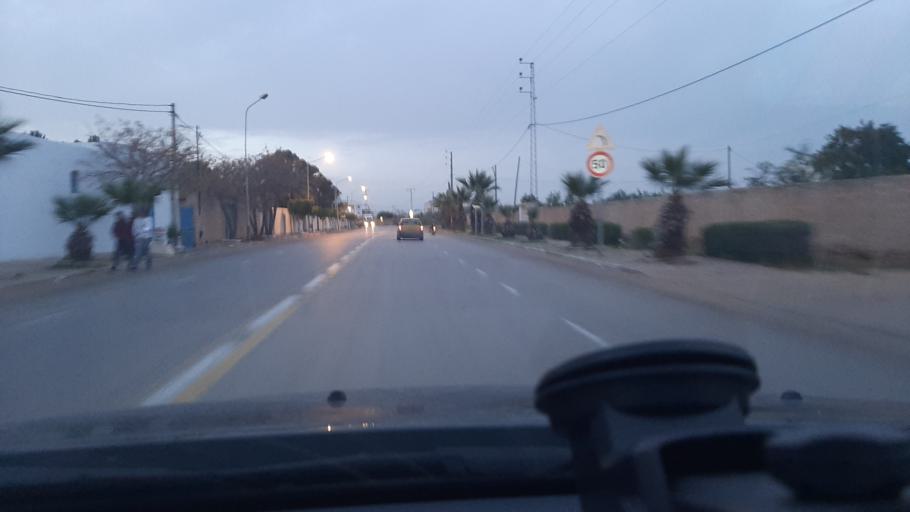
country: TN
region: Safaqis
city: Sfax
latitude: 34.7665
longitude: 10.6871
